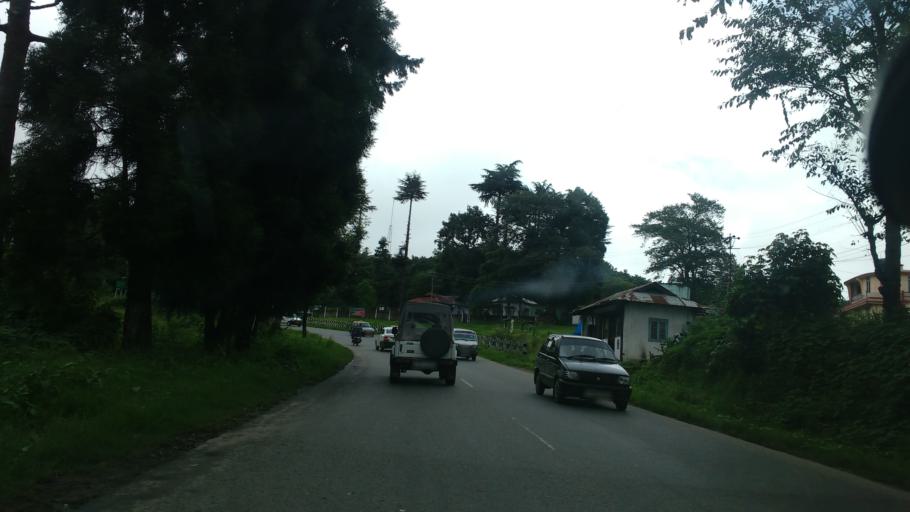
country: IN
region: Meghalaya
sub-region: East Khasi Hills
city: Shillong
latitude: 25.5501
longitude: 91.8419
